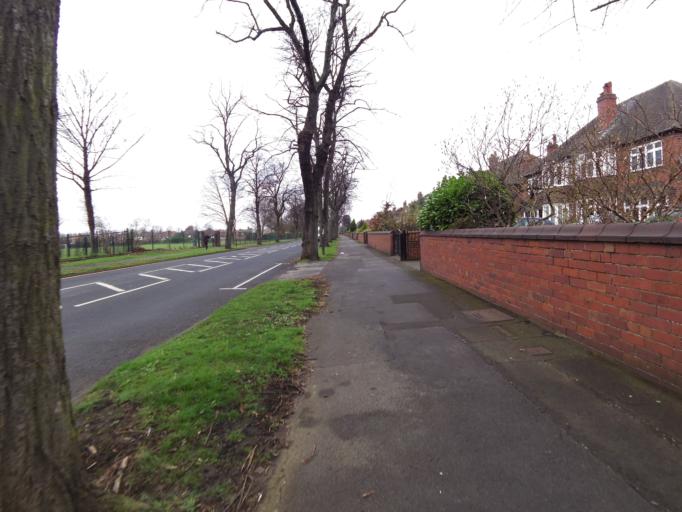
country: GB
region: England
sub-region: Doncaster
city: Doncaster
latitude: 53.5217
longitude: -1.1080
